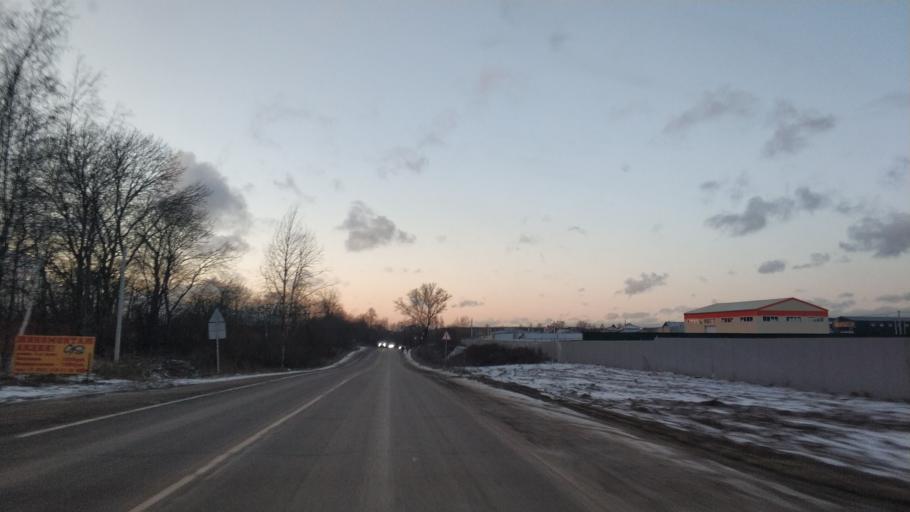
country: RU
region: St.-Petersburg
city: Pontonnyy
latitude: 59.8076
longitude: 30.6177
